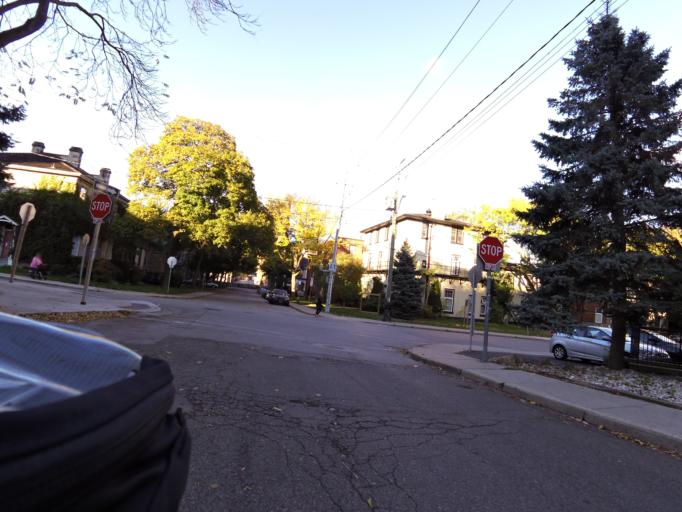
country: CA
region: Ontario
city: Hamilton
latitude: 43.2529
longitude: -79.8724
